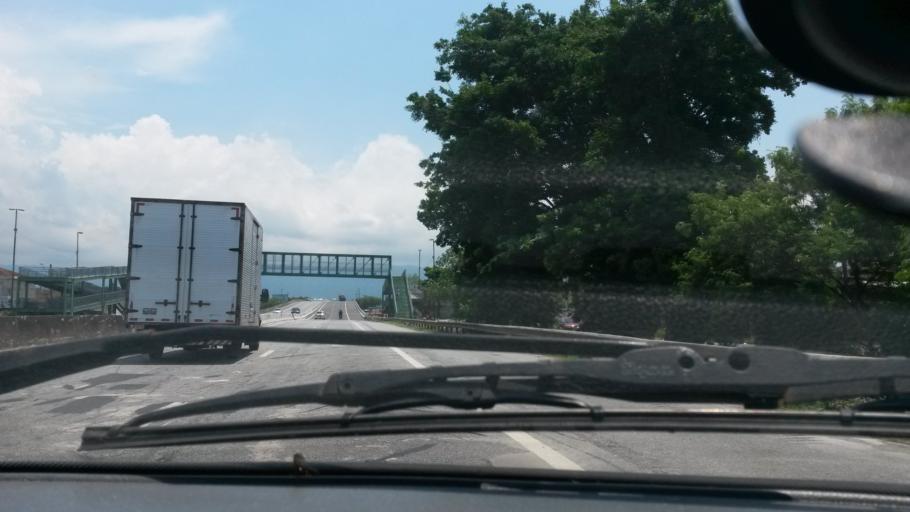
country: BR
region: Sao Paulo
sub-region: Sao Vicente
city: Sao Vicente
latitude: -23.9572
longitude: -46.4076
